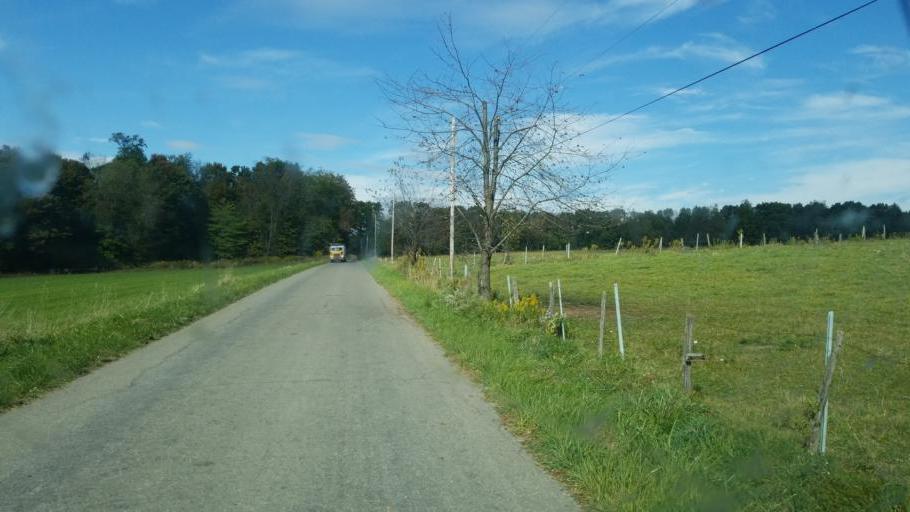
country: US
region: Pennsylvania
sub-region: Mercer County
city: Mercer
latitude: 41.3523
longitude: -80.2579
